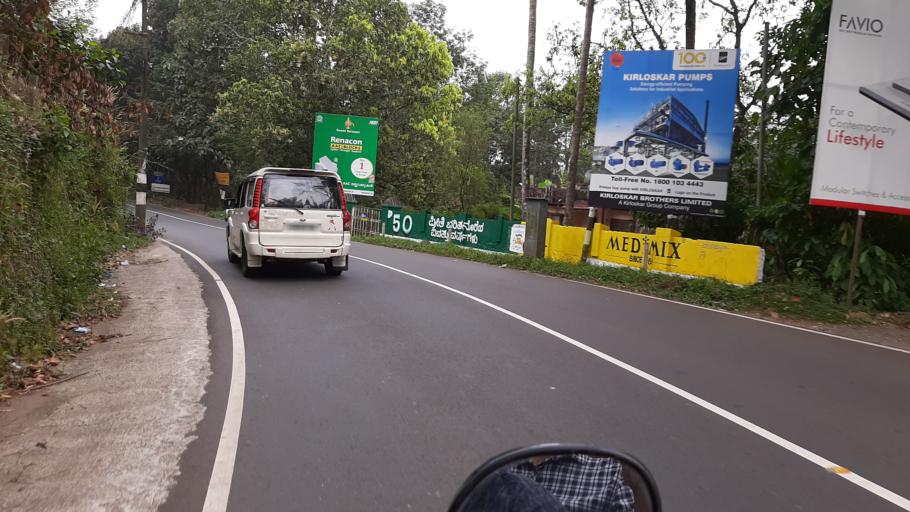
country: IN
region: Kerala
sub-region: Pattanamtitta
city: Pathanamthitta
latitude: 9.4509
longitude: 76.8703
